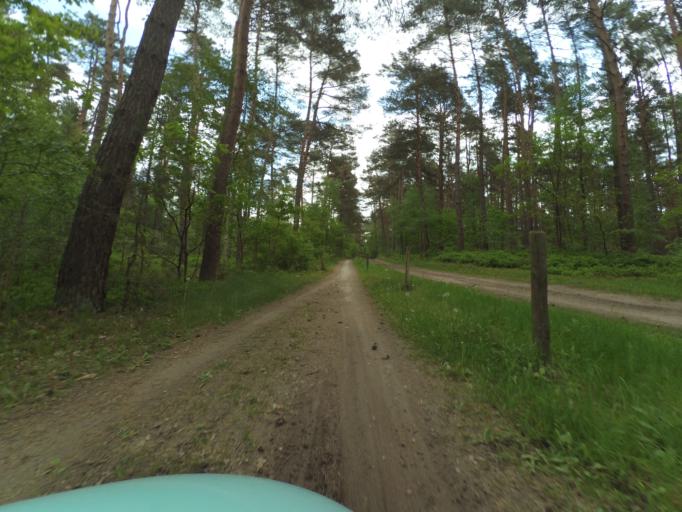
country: DE
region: Lower Saxony
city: Wietze
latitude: 52.6631
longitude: 9.7976
